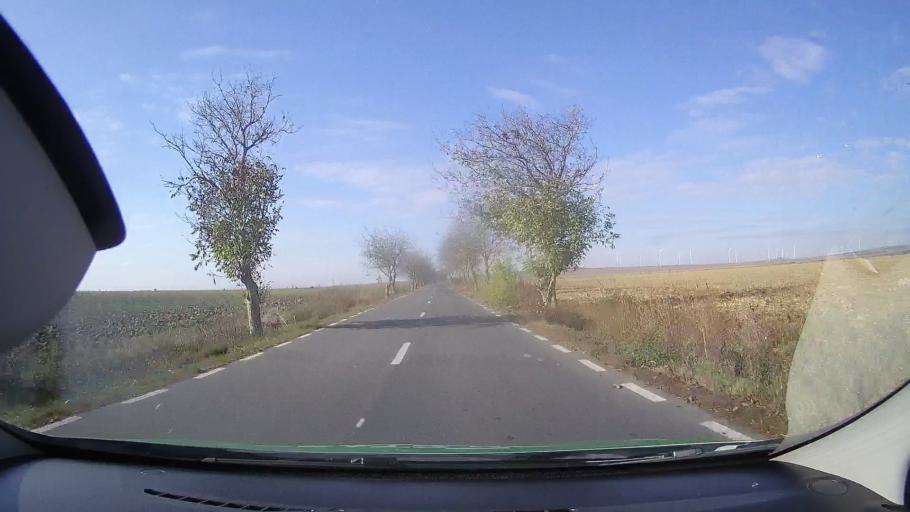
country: RO
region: Tulcea
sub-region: Comuna Bestepe
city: Bestepe
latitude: 45.0280
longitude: 29.0205
